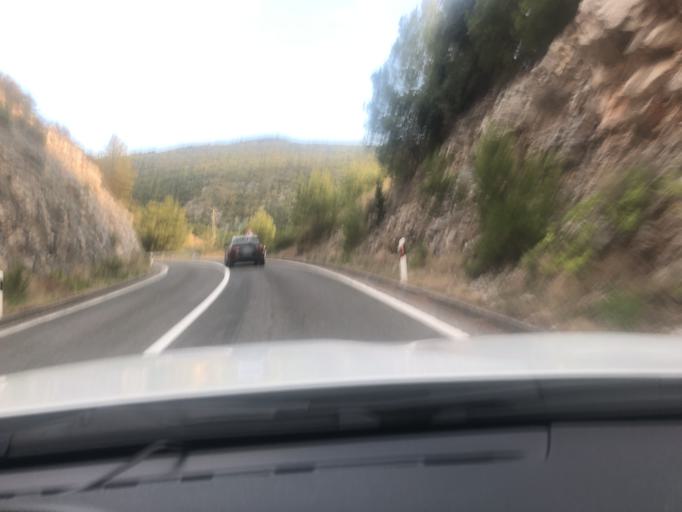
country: HR
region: Splitsko-Dalmatinska
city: Stari Grad
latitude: 43.1699
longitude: 16.5633
